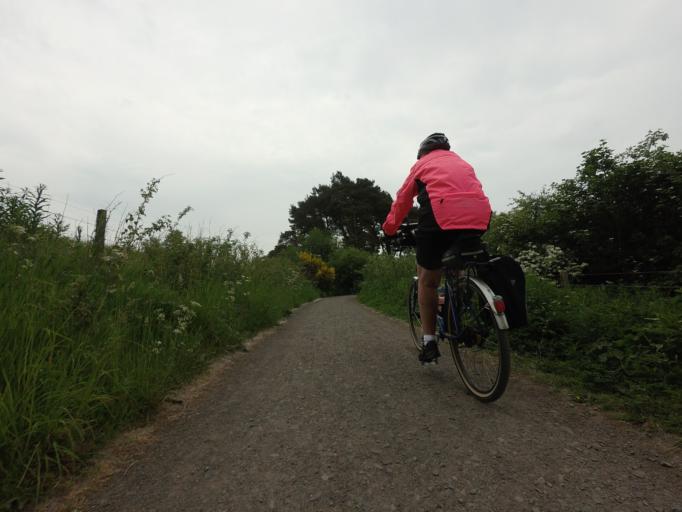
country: GB
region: Scotland
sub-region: Perth and Kinross
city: Milnathort
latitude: 56.2193
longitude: -3.3886
